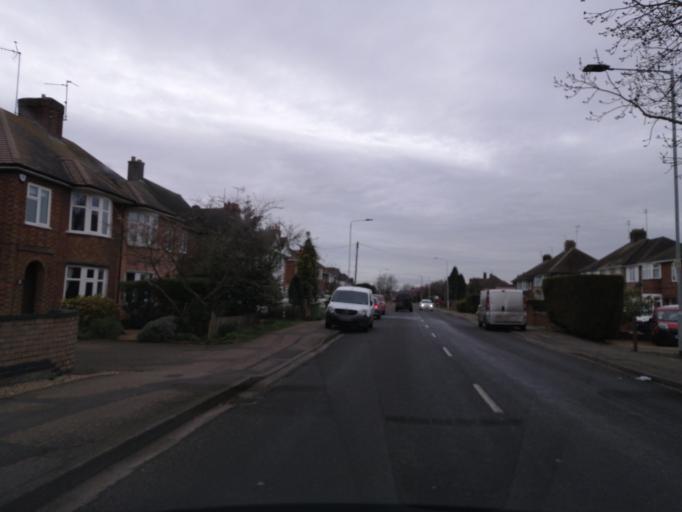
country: GB
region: England
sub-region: Peterborough
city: Peterborough
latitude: 52.5907
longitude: -0.2277
